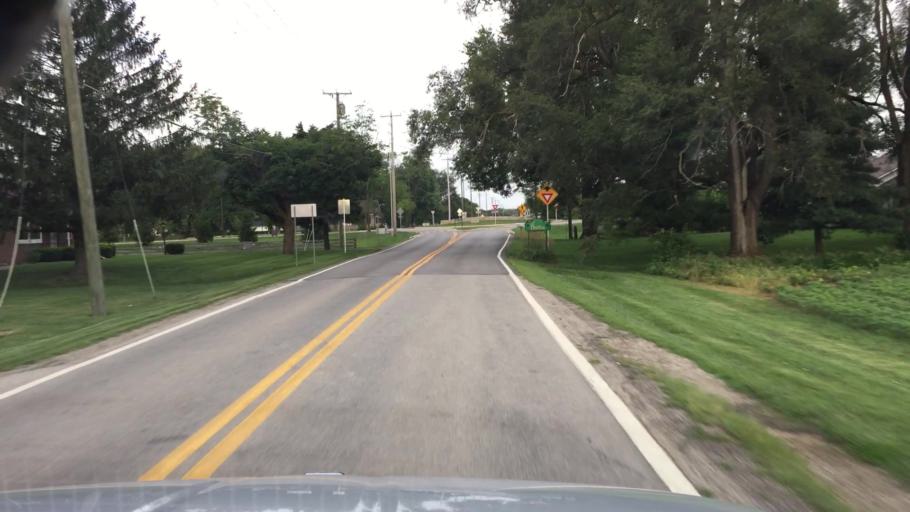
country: US
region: Ohio
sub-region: Franklin County
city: Hilliard
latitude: 40.0771
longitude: -83.1770
